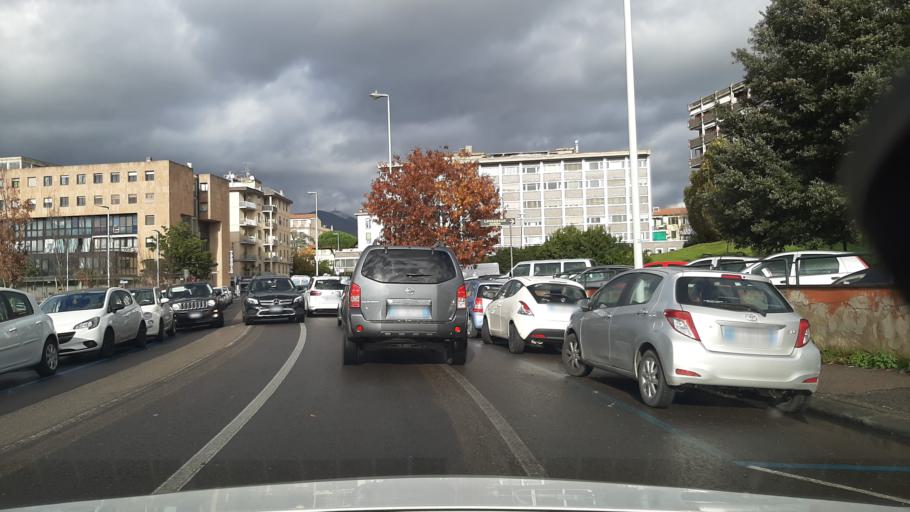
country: IT
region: Tuscany
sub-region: Province of Florence
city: Florence
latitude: 43.7958
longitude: 11.2447
